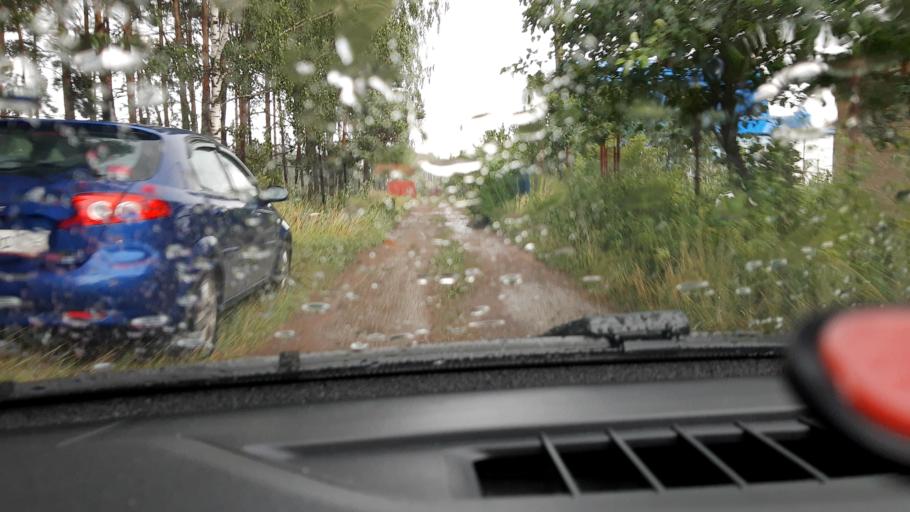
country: RU
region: Nizjnij Novgorod
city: Lukino
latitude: 56.3883
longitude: 43.6660
